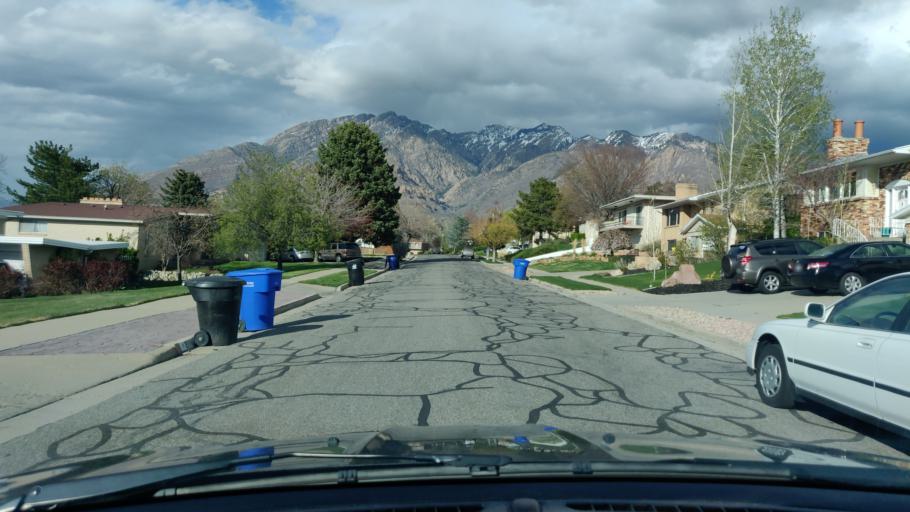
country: US
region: Utah
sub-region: Salt Lake County
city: Cottonwood Heights
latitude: 40.6181
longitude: -111.8229
